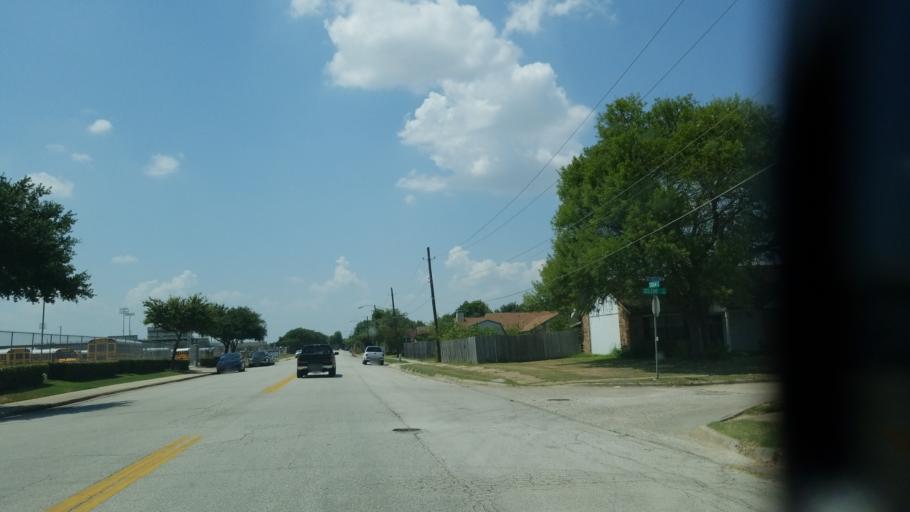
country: US
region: Texas
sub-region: Dallas County
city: Garland
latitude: 32.9265
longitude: -96.6312
